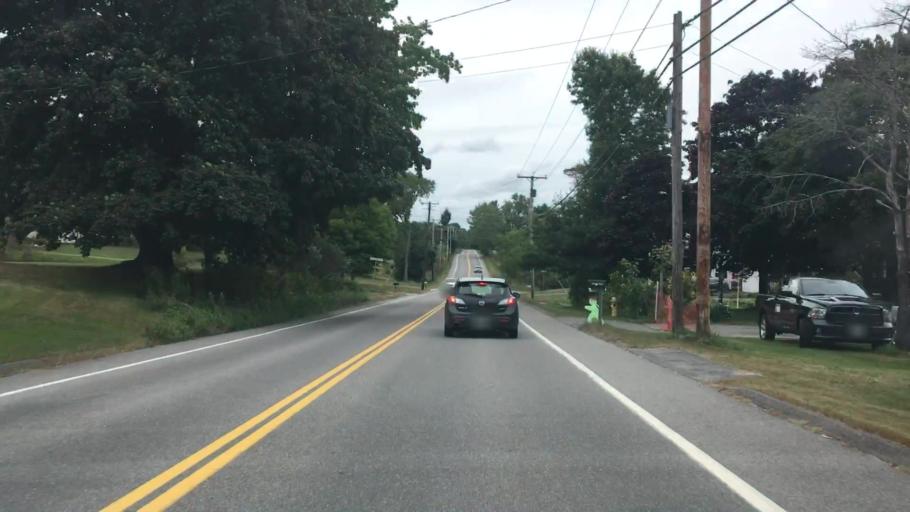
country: US
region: Maine
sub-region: Cumberland County
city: Yarmouth
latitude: 43.8245
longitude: -70.1918
